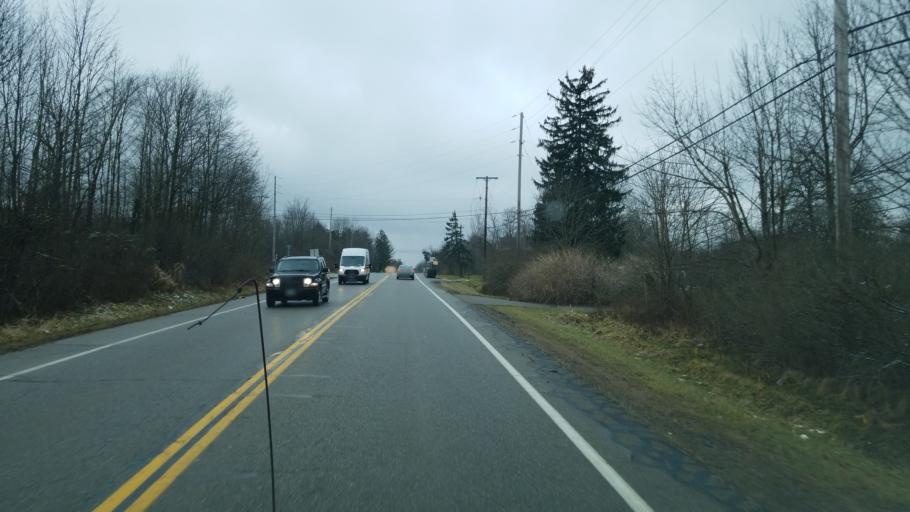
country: US
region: Ohio
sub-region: Portage County
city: Streetsboro
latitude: 41.2398
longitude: -81.3910
